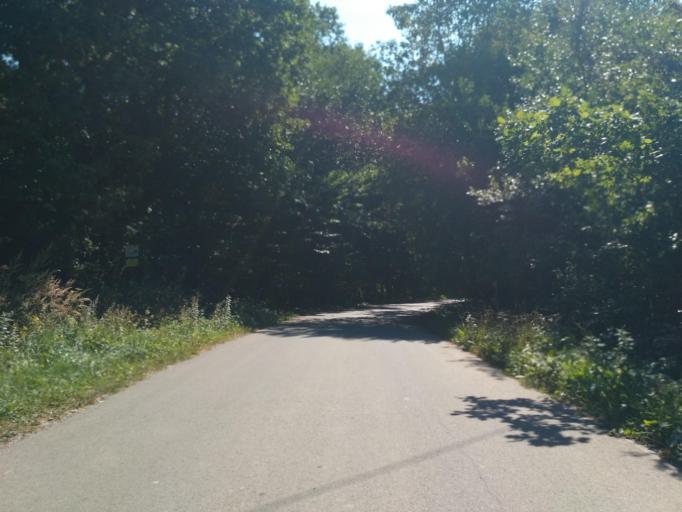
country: PL
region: Subcarpathian Voivodeship
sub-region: Powiat brzozowski
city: Niebocko
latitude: 49.6497
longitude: 22.1300
